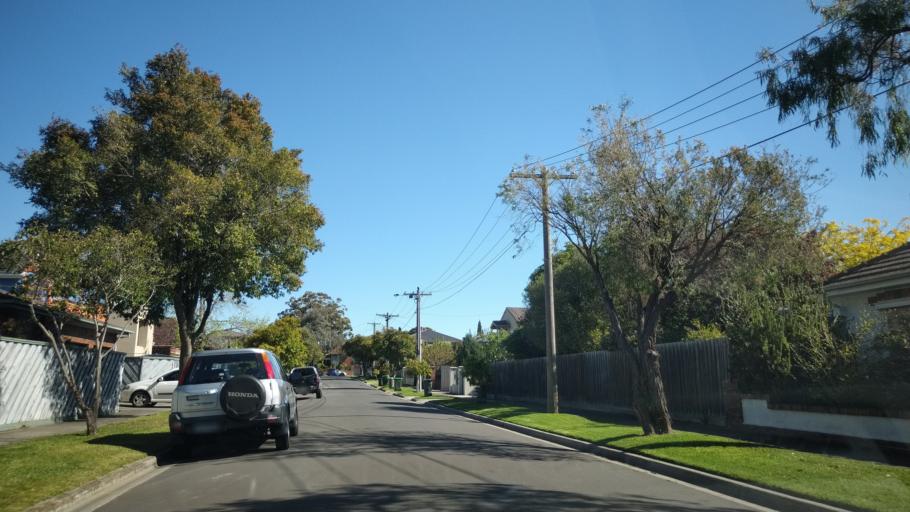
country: AU
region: Victoria
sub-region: Bayside
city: Brighton East
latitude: -37.9046
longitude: 145.0244
